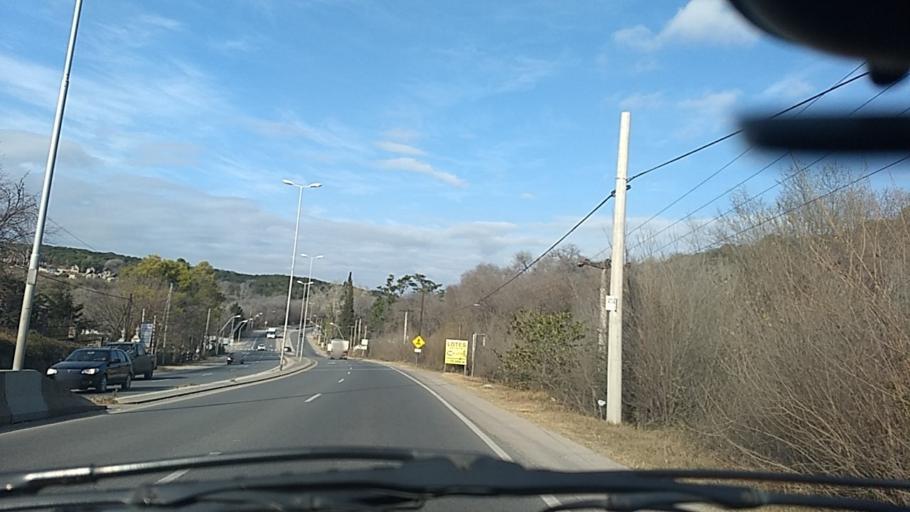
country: AR
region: Cordoba
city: Salsipuedes
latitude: -31.1515
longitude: -64.2990
